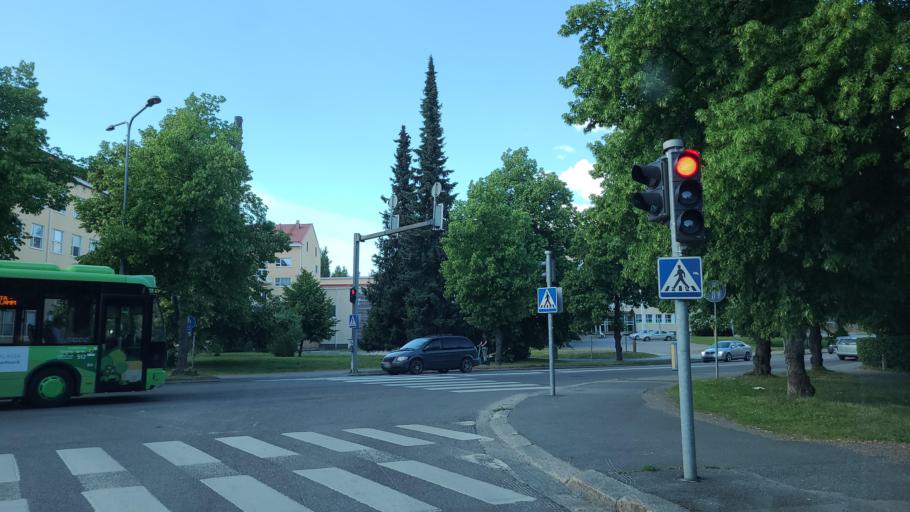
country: FI
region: Central Finland
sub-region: Jyvaeskylae
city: Jyvaeskylae
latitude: 62.2503
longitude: 25.7441
